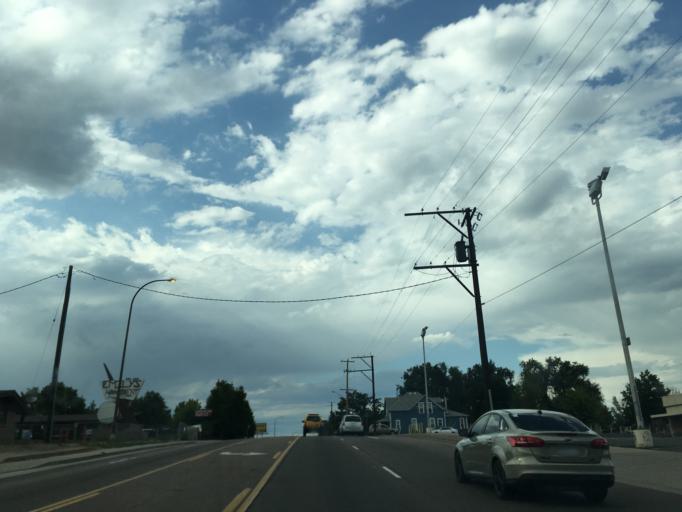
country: US
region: Colorado
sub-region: Jefferson County
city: Lakewood
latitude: 39.7194
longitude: -105.0533
